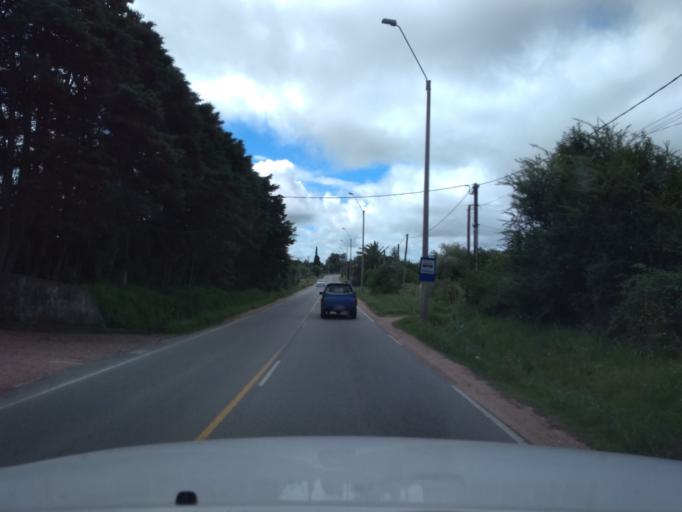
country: UY
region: Canelones
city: Pando
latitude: -34.6983
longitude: -55.9669
